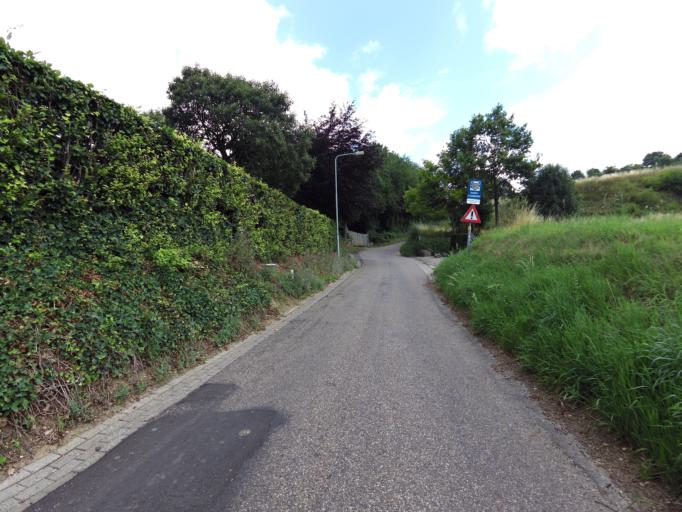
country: NL
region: Limburg
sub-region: Gemeente Voerendaal
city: Ubachsberg
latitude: 50.8135
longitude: 5.9406
